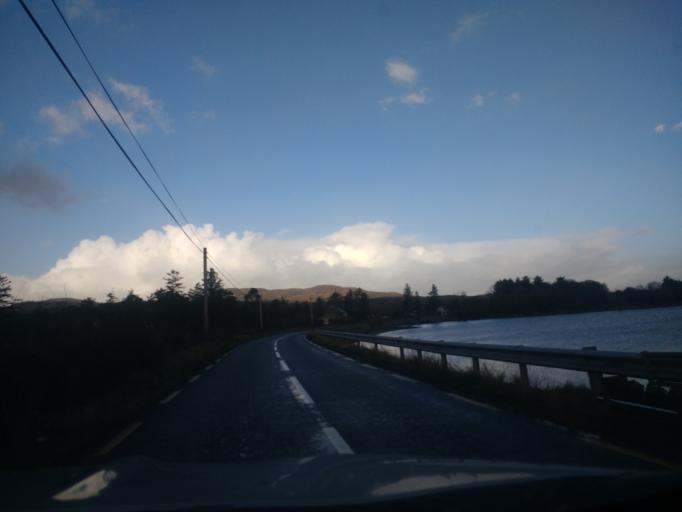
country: IE
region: Ulster
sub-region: County Donegal
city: Ramelton
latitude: 55.0712
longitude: -7.5989
